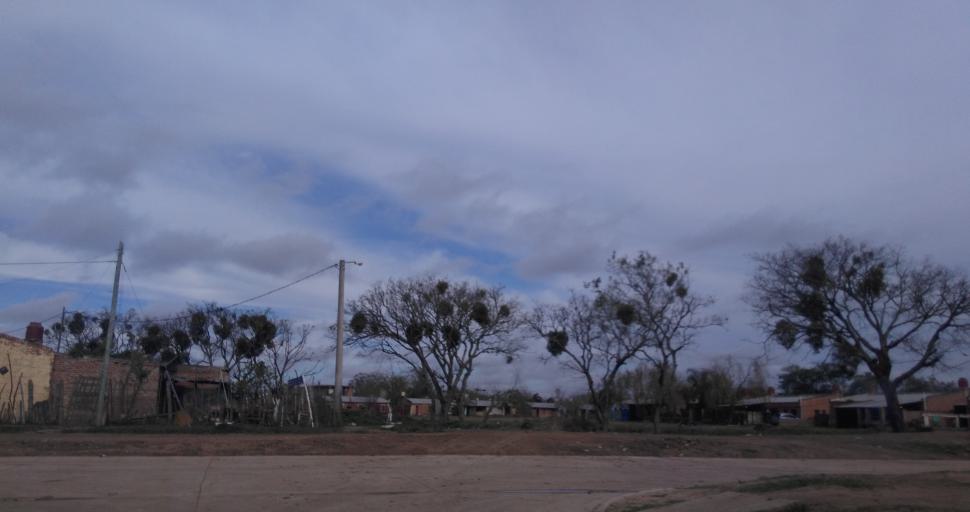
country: AR
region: Chaco
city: Fontana
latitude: -27.3966
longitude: -58.9901
